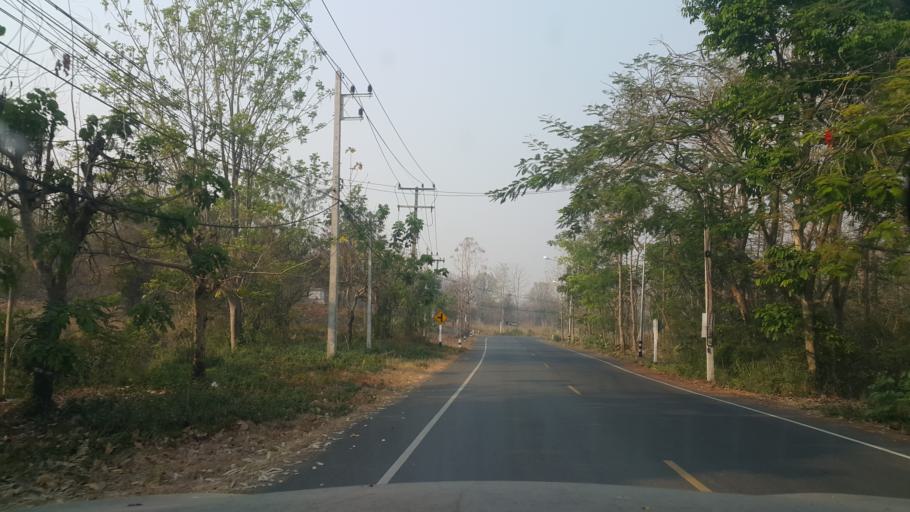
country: TH
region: Chiang Mai
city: Mae On
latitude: 18.7764
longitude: 99.2456
